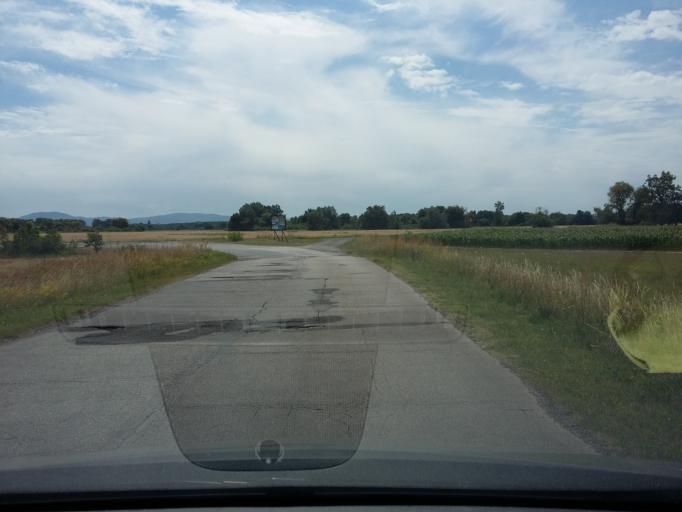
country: SK
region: Bratislavsky
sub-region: Okres Malacky
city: Malacky
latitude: 48.4919
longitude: 16.9667
